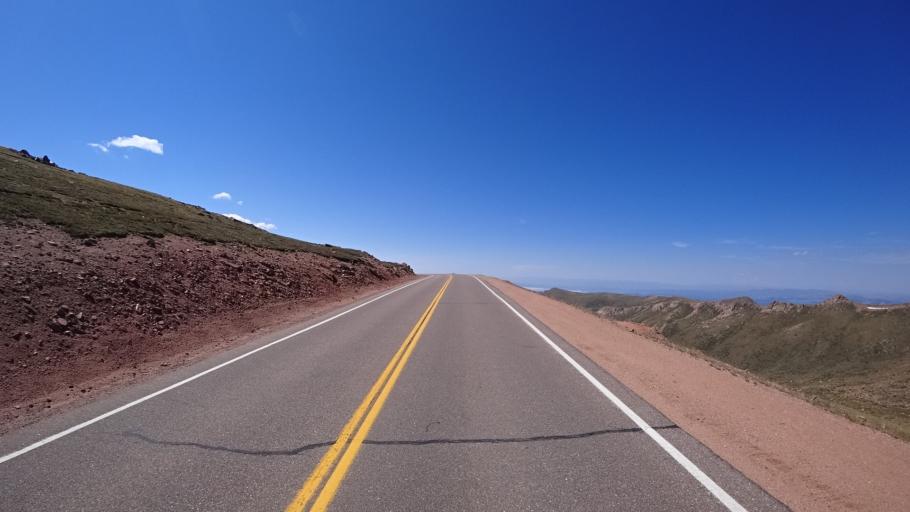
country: US
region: Colorado
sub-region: El Paso County
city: Cascade-Chipita Park
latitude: 38.8606
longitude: -105.0678
